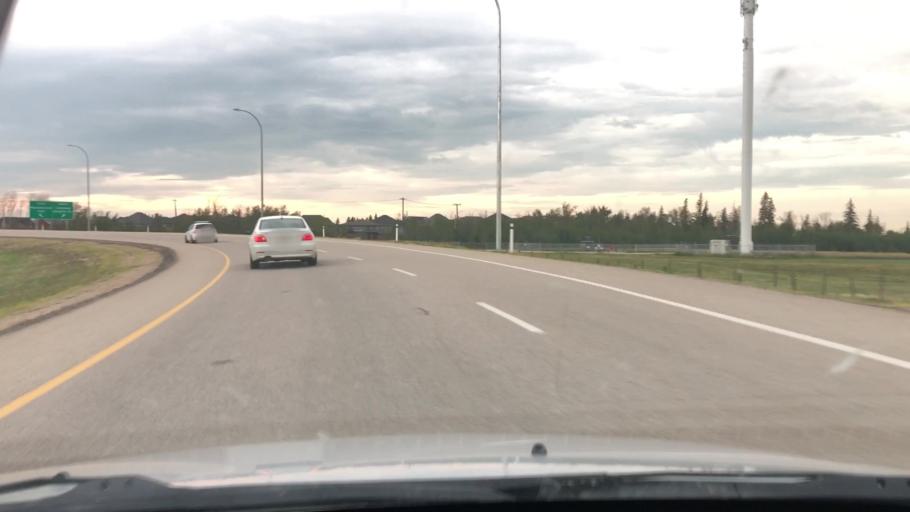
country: CA
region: Alberta
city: Devon
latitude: 53.4667
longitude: -113.6247
